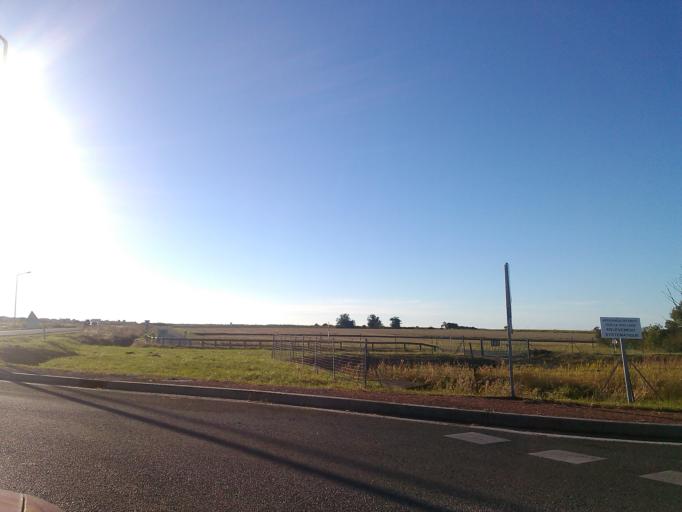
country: FR
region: Poitou-Charentes
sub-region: Departement de la Charente-Maritime
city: Etaules
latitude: 45.7415
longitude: -1.0920
